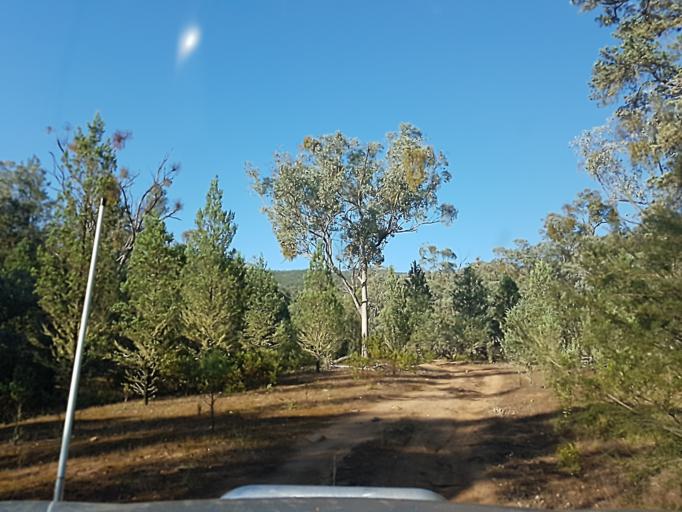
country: AU
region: New South Wales
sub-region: Snowy River
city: Jindabyne
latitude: -36.9440
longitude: 148.3839
